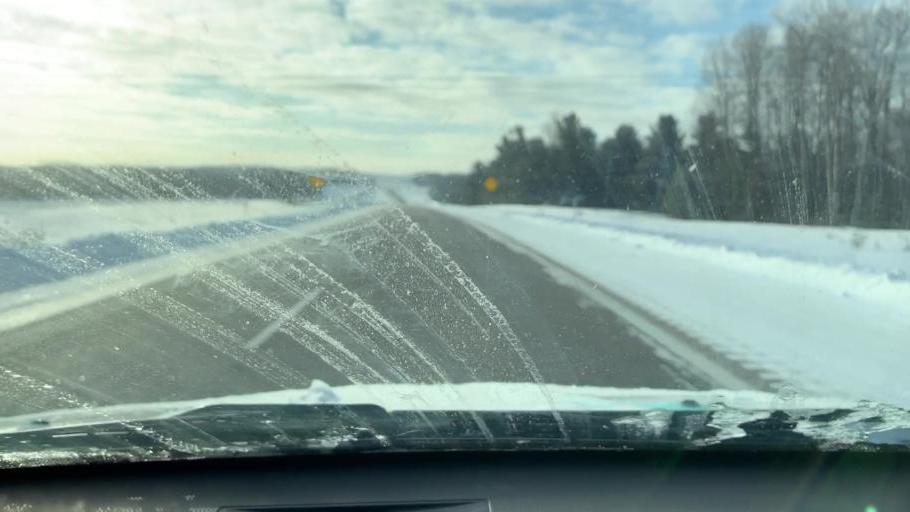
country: US
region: Michigan
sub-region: Wexford County
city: Cadillac
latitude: 44.3301
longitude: -85.4053
